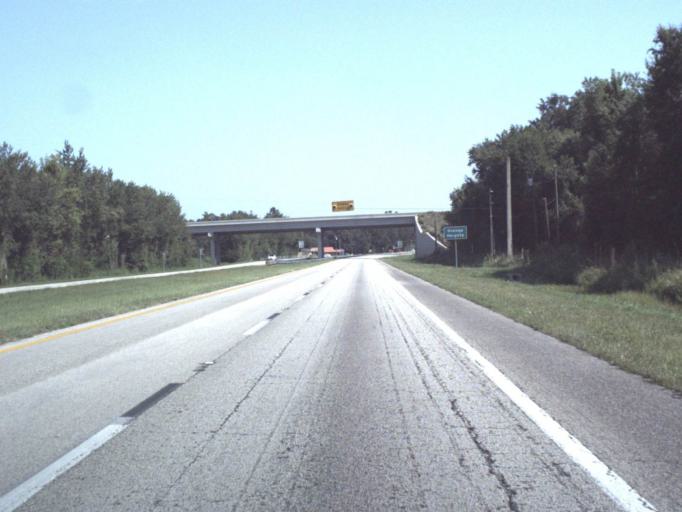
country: US
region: Florida
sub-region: Alachua County
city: Waldo
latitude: 29.7126
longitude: -82.1381
